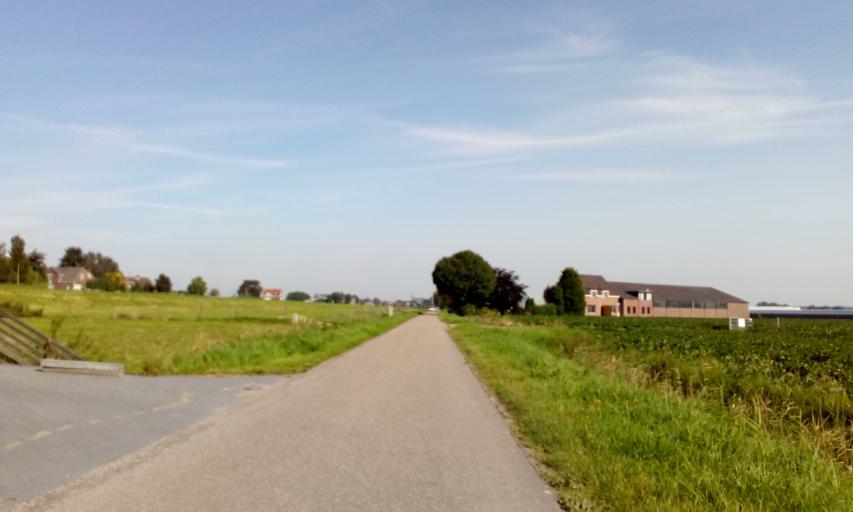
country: NL
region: South Holland
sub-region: Gemeente Lansingerland
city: Bleiswijk
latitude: 52.0317
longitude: 4.5795
